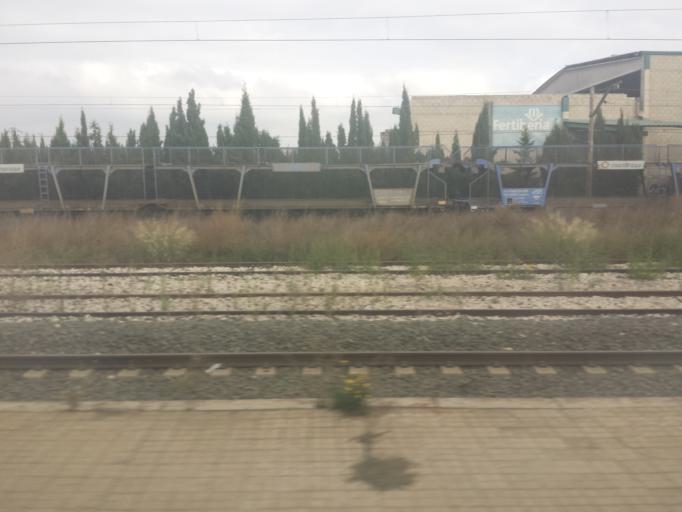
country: ES
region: Aragon
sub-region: Provincia de Zaragoza
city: Sobradiel
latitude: 41.7232
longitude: -1.0205
